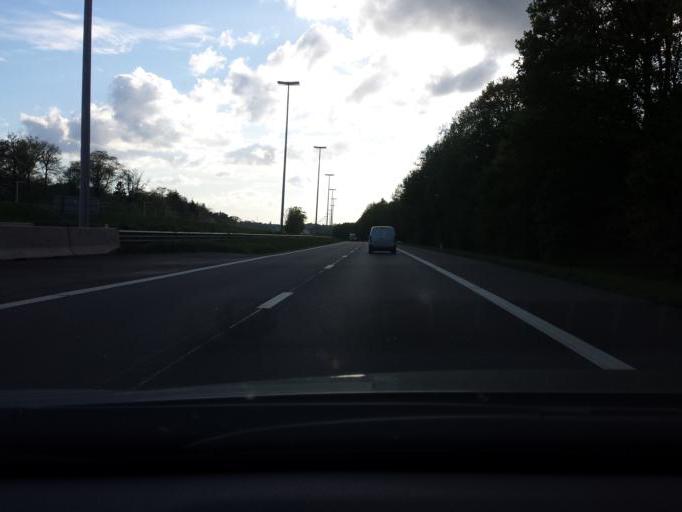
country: BE
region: Wallonia
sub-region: Province de Liege
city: Limbourg
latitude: 50.6498
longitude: 5.9312
